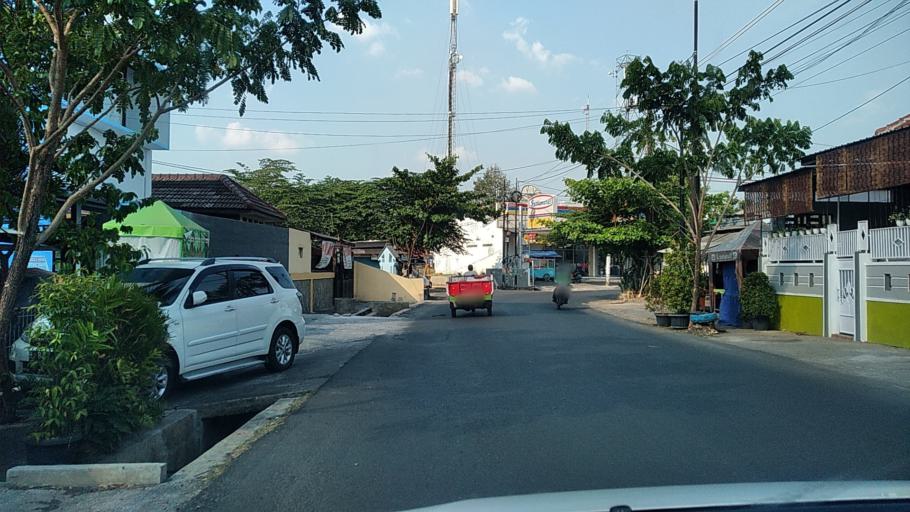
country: ID
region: Central Java
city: Ungaran
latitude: -7.0696
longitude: 110.4249
